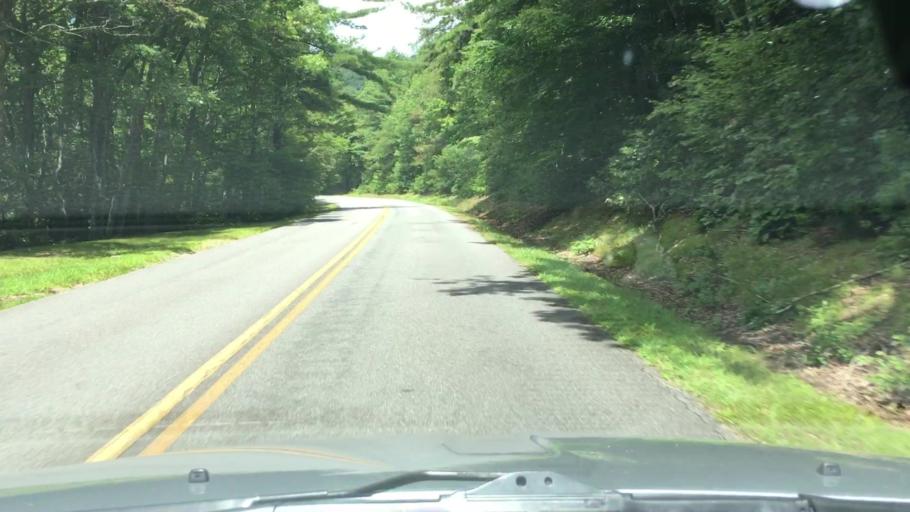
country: US
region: North Carolina
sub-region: Buncombe County
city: Asheville
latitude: 35.6268
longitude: -82.4927
